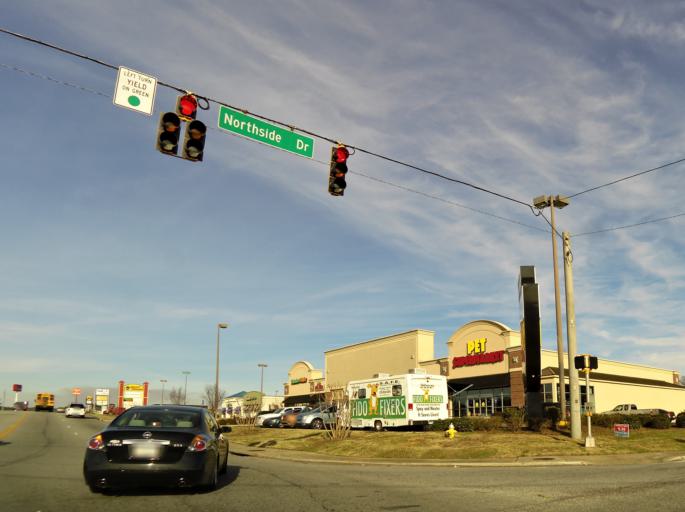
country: US
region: Georgia
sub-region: Bibb County
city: Macon
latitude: 32.8966
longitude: -83.6908
